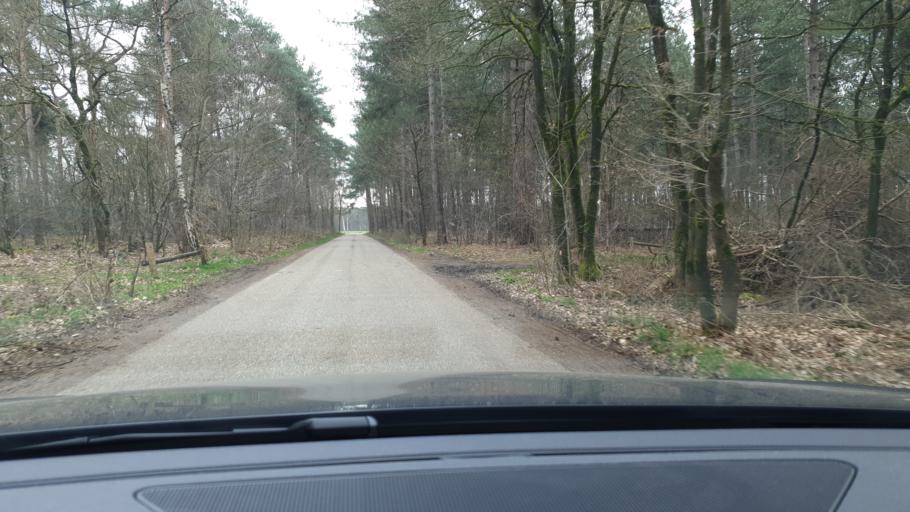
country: NL
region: North Brabant
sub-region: Gemeente Oirschot
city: Middelbeers
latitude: 51.4284
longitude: 5.2642
